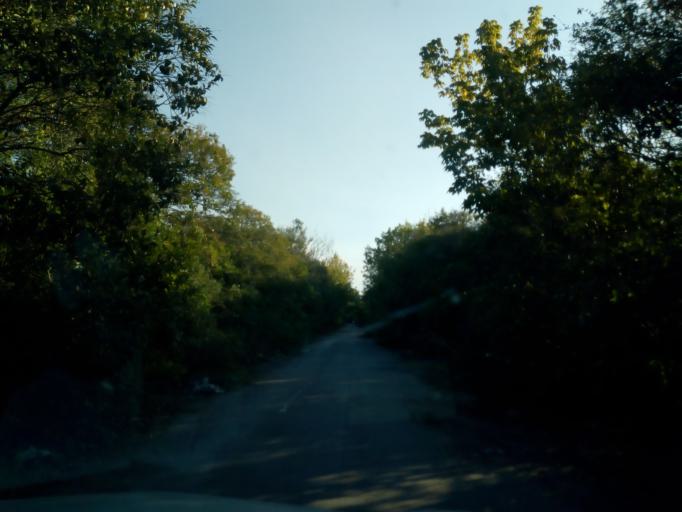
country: AR
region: Buenos Aires
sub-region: Partido de Ensenada
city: Ensenada
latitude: -34.7835
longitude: -58.0137
